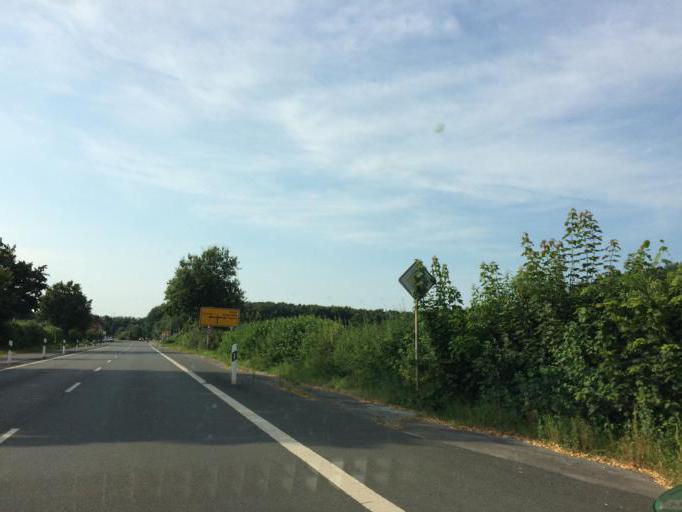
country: DE
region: North Rhine-Westphalia
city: Dorsten
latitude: 51.6797
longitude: 7.0181
